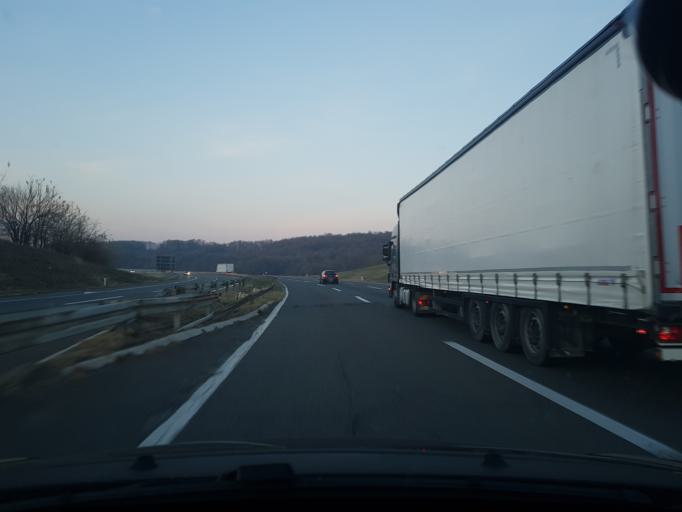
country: RS
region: Central Serbia
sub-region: Nisavski Okrug
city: Razanj
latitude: 43.6924
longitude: 21.5474
